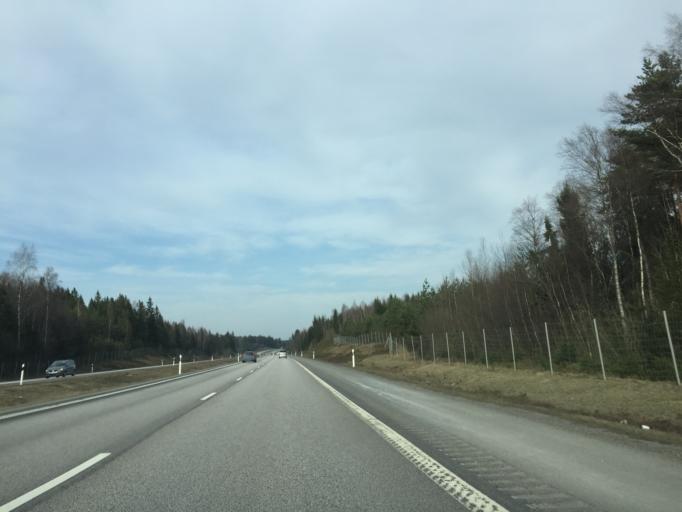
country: SE
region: OErebro
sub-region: Lindesbergs Kommun
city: Fellingsbro
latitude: 59.3572
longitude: 15.5662
